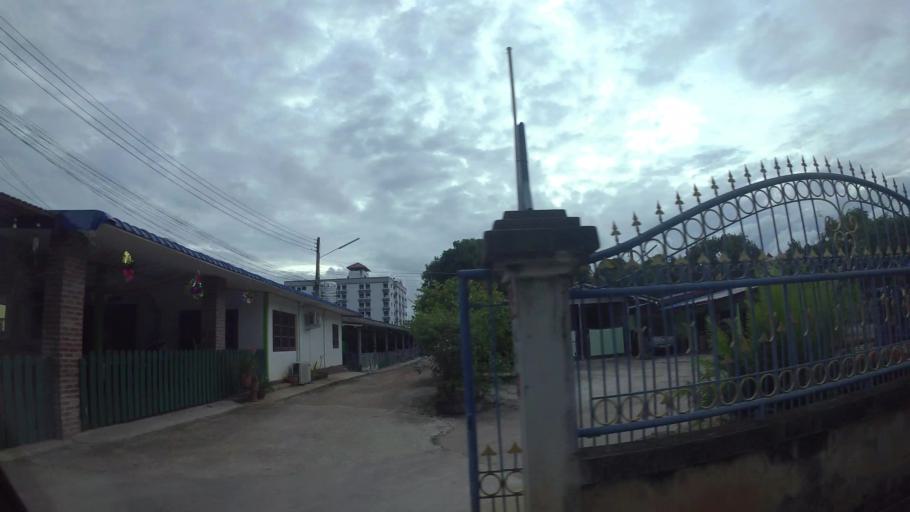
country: TH
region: Rayong
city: Rayong
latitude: 12.6780
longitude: 101.2645
